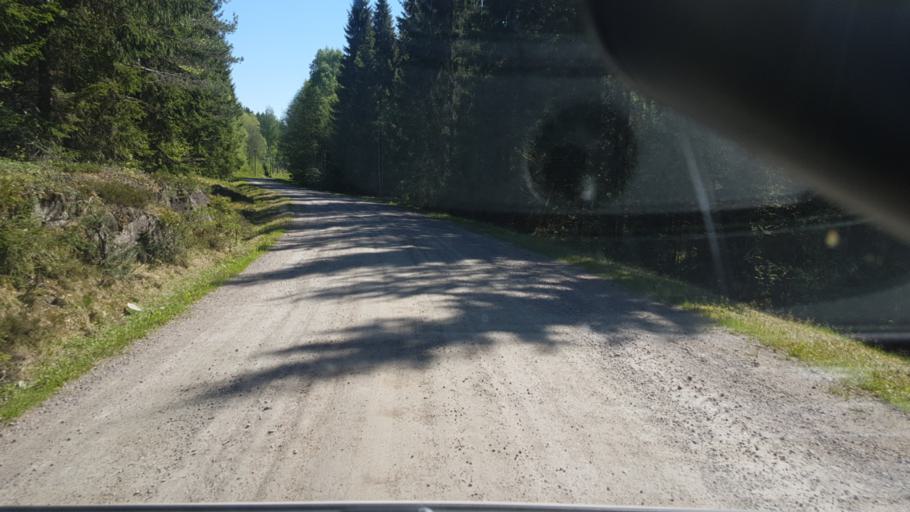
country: SE
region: Vaermland
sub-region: Eda Kommun
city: Charlottenberg
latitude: 59.9337
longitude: 12.3709
